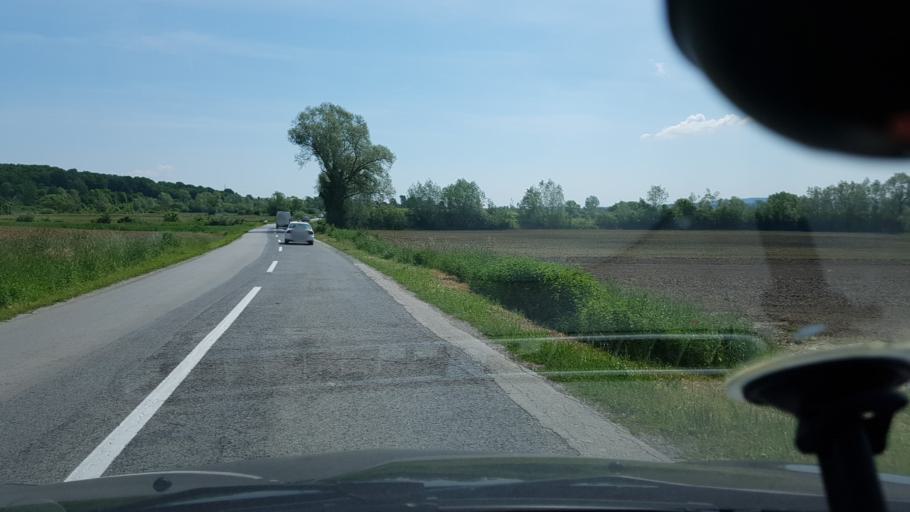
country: HR
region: Krapinsko-Zagorska
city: Selnica
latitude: 46.0530
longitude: 16.0452
